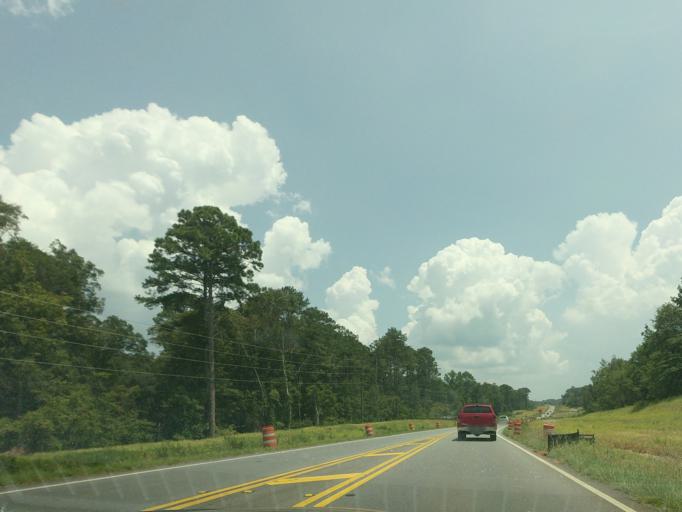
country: US
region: Georgia
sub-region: Houston County
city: Robins Air Force Base
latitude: 32.5532
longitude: -83.6163
